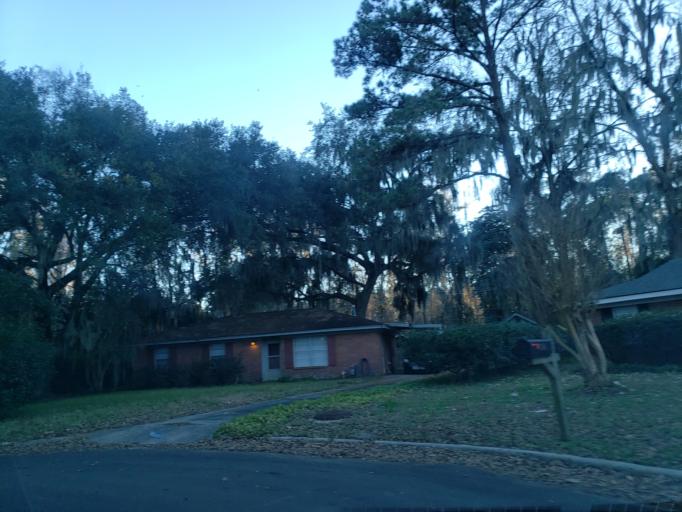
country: US
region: Georgia
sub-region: Chatham County
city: Isle of Hope
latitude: 31.9761
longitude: -81.0992
